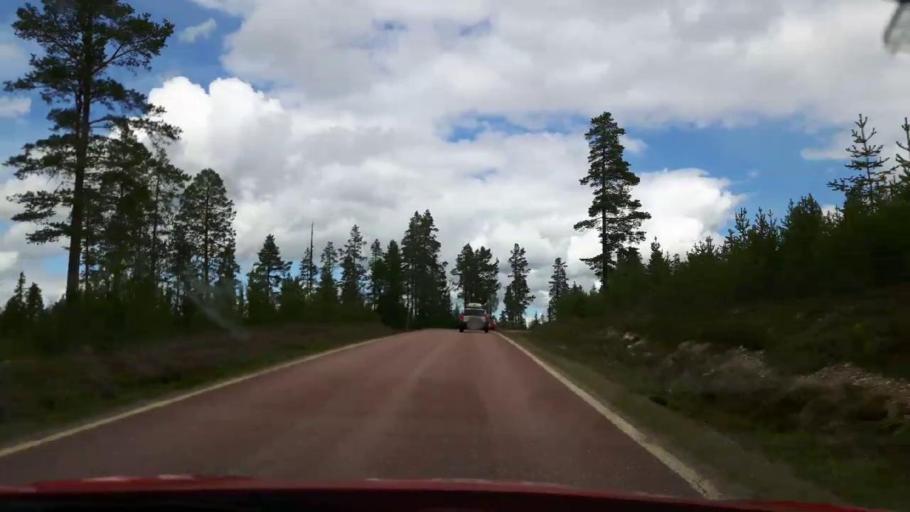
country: NO
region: Hedmark
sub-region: Trysil
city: Innbygda
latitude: 61.8726
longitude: 12.9611
